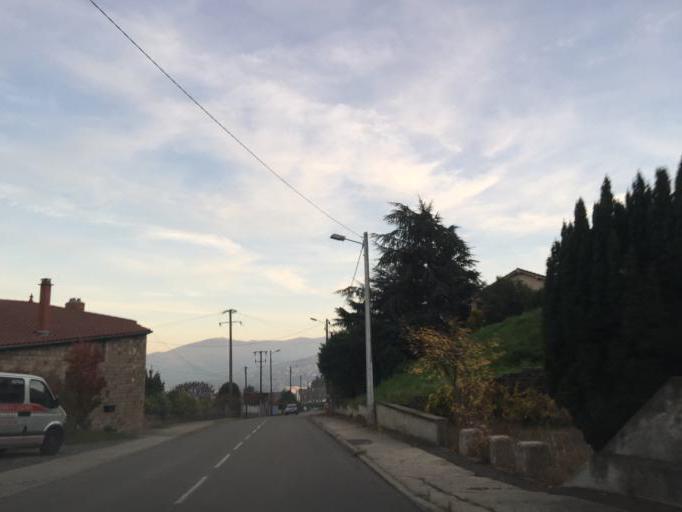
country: FR
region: Rhone-Alpes
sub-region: Departement de la Loire
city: Saint-Chamond
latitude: 45.4840
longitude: 4.5020
